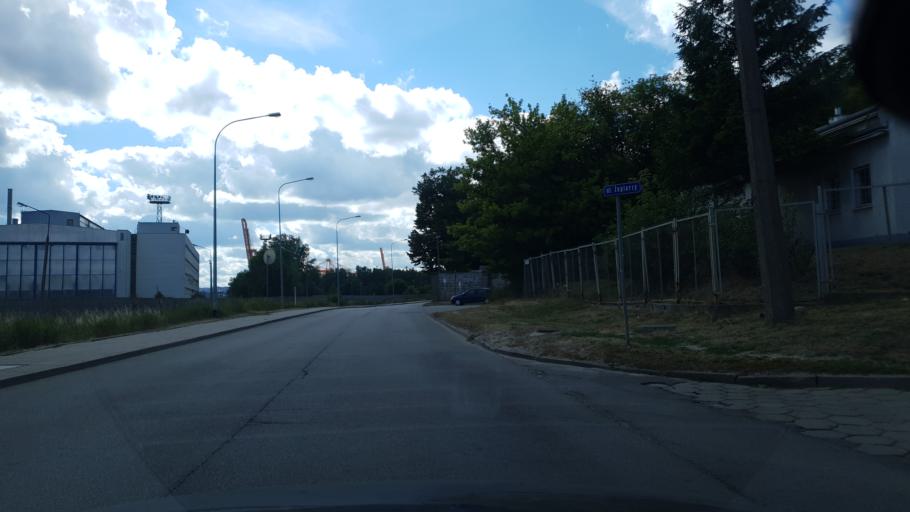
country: PL
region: Pomeranian Voivodeship
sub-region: Gdynia
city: Gdynia
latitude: 54.5431
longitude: 18.5303
